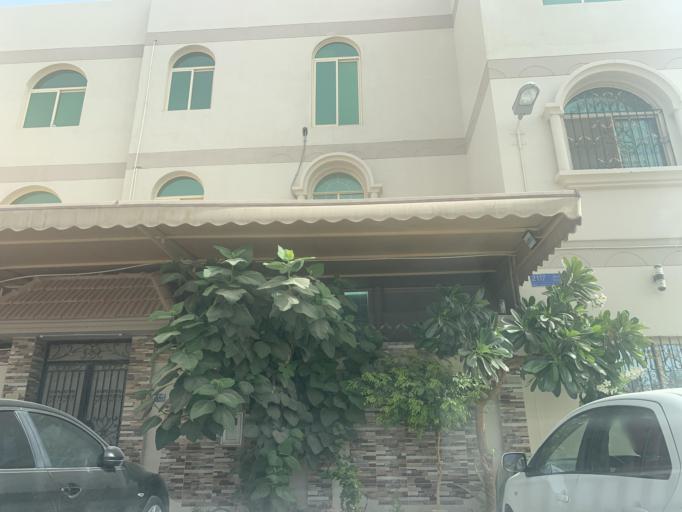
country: BH
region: Manama
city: Jidd Hafs
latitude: 26.2179
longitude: 50.5433
